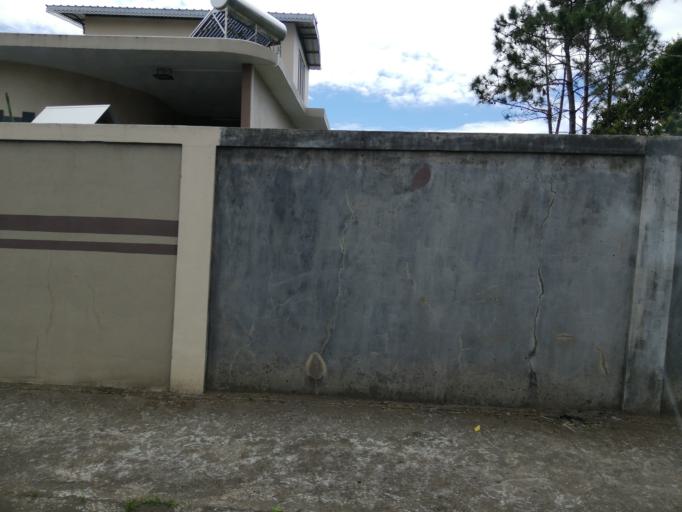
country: MU
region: Moka
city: Melrose
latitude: -20.2693
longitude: 57.6347
